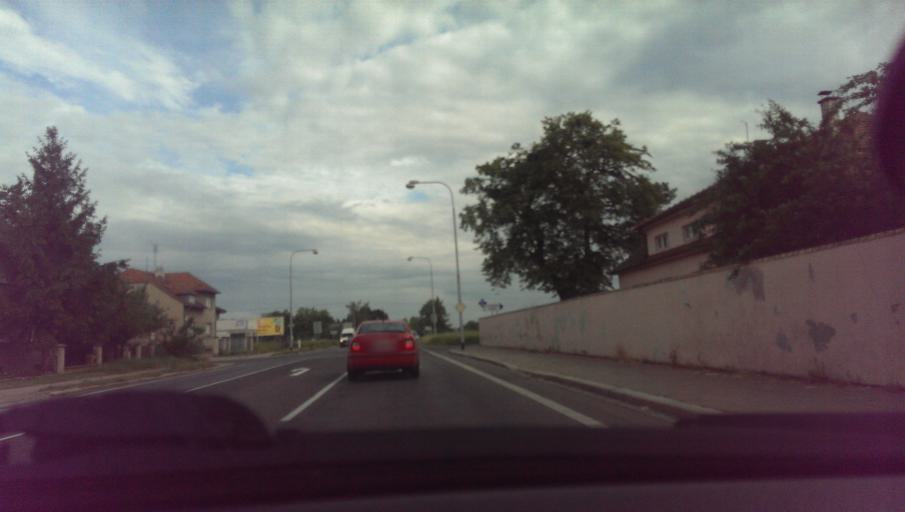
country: CZ
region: Zlin
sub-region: Okres Kromeriz
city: Kromeriz
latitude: 49.3047
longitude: 17.3820
